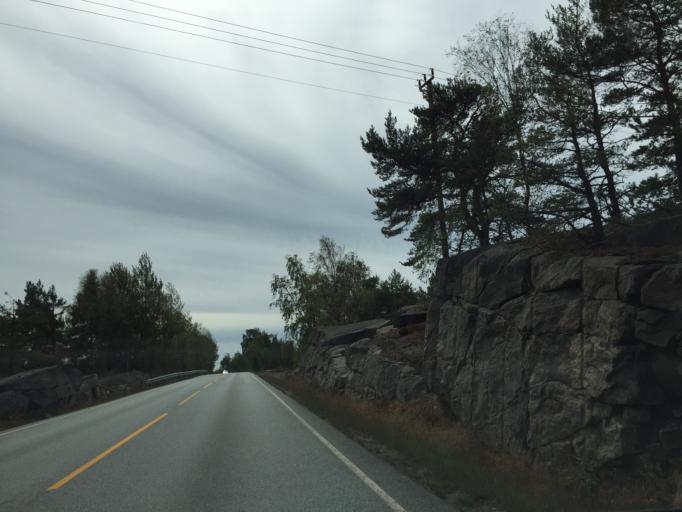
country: NO
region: Ostfold
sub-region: Fredrikstad
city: Fredrikstad
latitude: 59.0919
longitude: 10.9271
